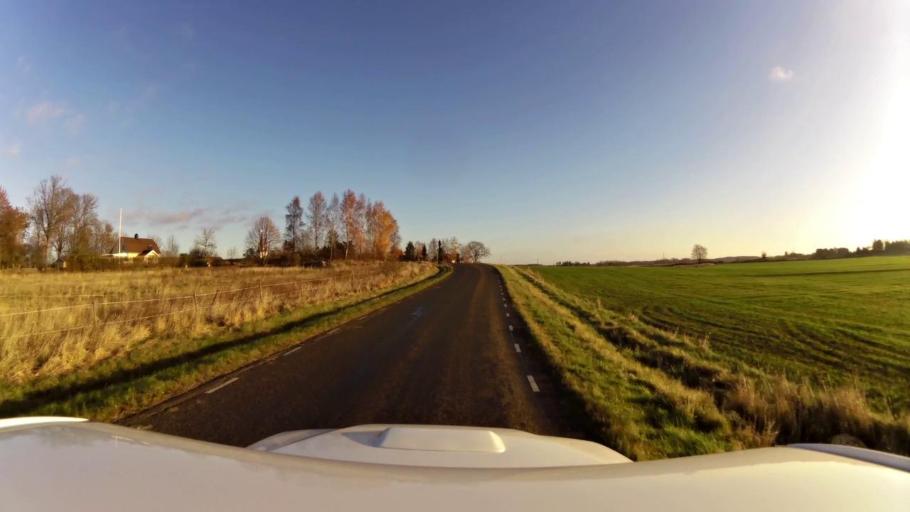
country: SE
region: OEstergoetland
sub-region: Linkopings Kommun
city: Linghem
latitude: 58.4853
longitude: 15.7418
